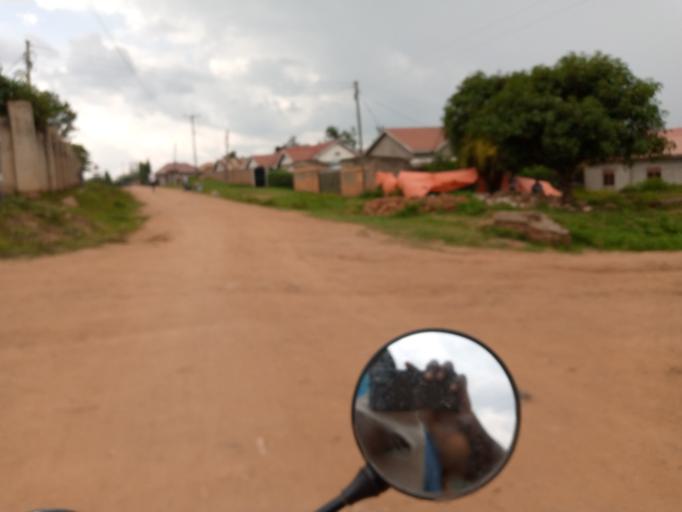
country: UG
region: Eastern Region
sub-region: Mbale District
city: Mbale
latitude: 1.0874
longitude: 34.1713
